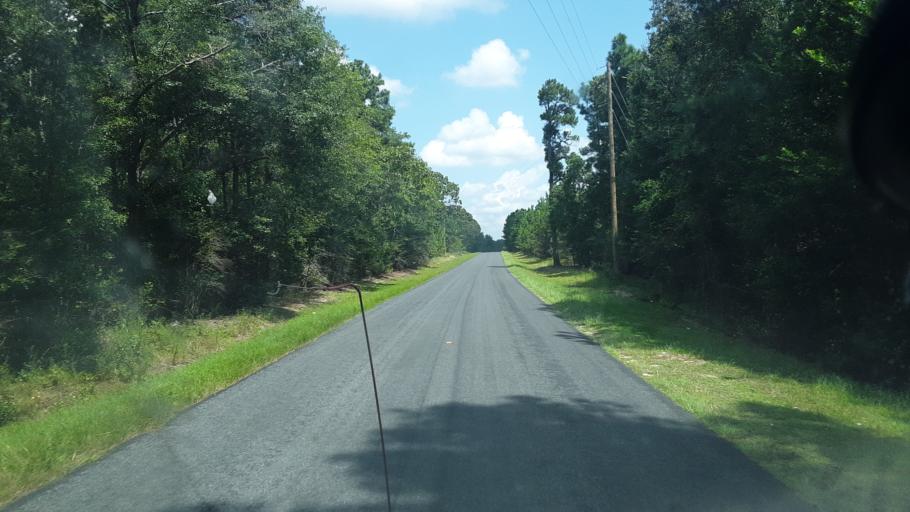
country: US
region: South Carolina
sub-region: Calhoun County
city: Oak Grove
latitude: 33.6995
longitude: -80.9615
